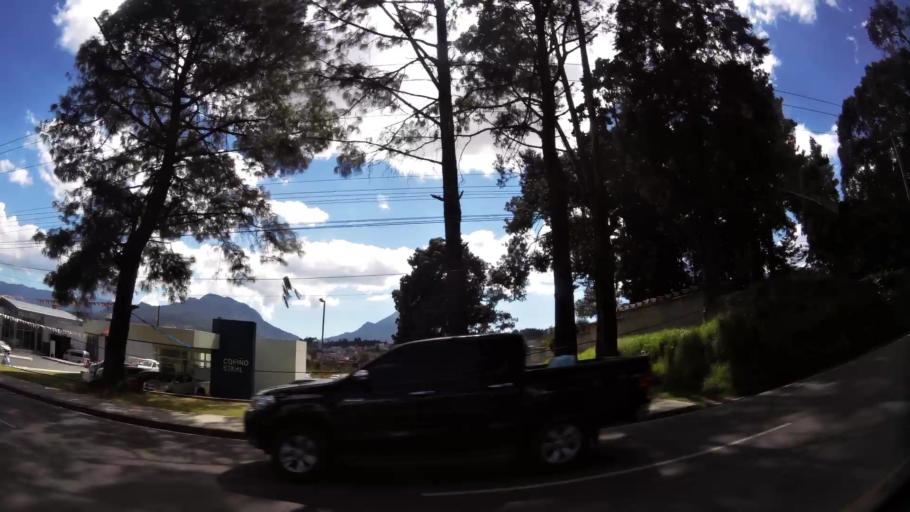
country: GT
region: Quetzaltenango
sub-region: Municipio de La Esperanza
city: La Esperanza
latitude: 14.8590
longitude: -91.5444
